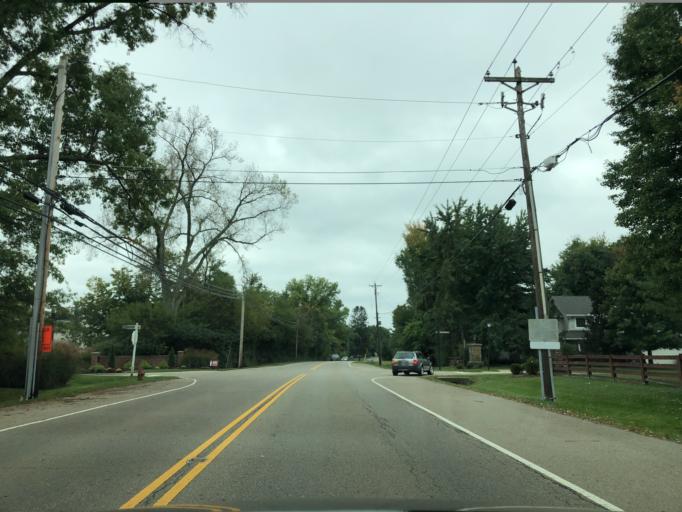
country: US
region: Ohio
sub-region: Warren County
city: Landen
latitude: 39.2945
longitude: -84.2804
